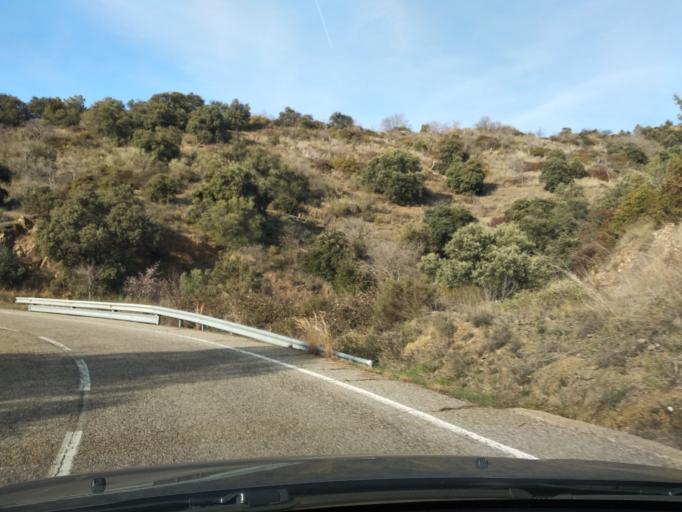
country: ES
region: Catalonia
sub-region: Provincia de Tarragona
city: Falset
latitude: 41.2092
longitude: 0.7759
